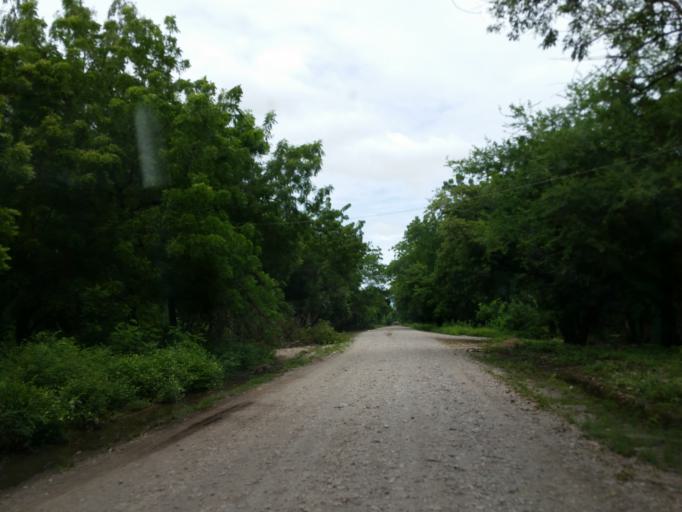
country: NI
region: Leon
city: Telica
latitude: 12.7084
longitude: -86.8723
